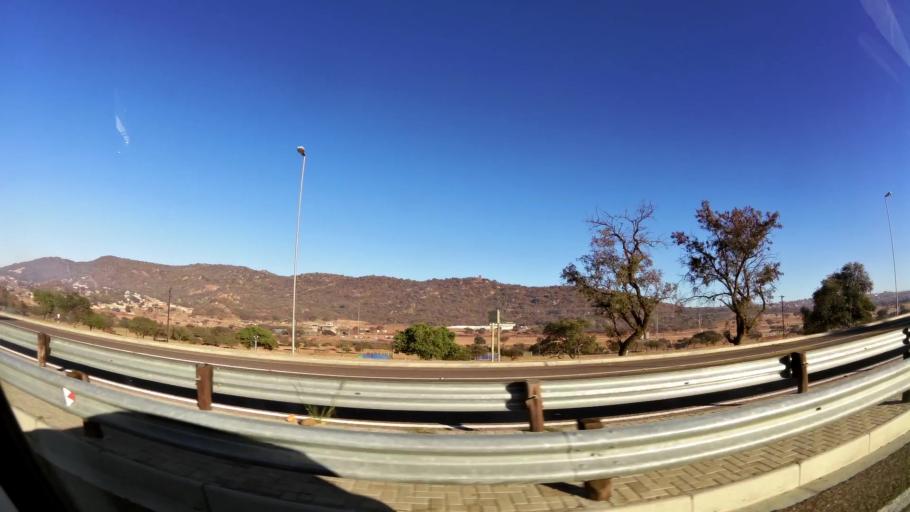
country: ZA
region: Limpopo
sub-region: Capricorn District Municipality
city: Mankoeng
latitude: -23.9315
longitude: 29.7951
